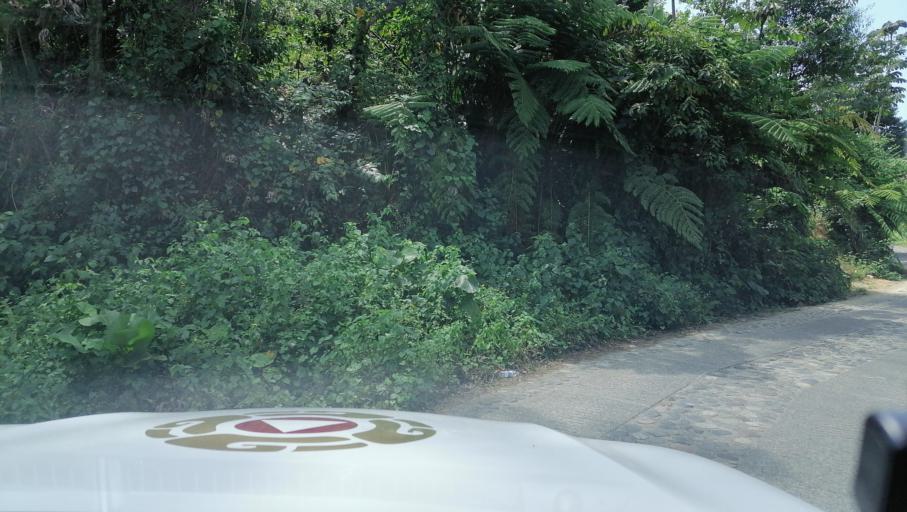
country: MX
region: Chiapas
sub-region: Tapachula
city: Canton Villaflor
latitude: 15.1374
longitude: -92.2873
